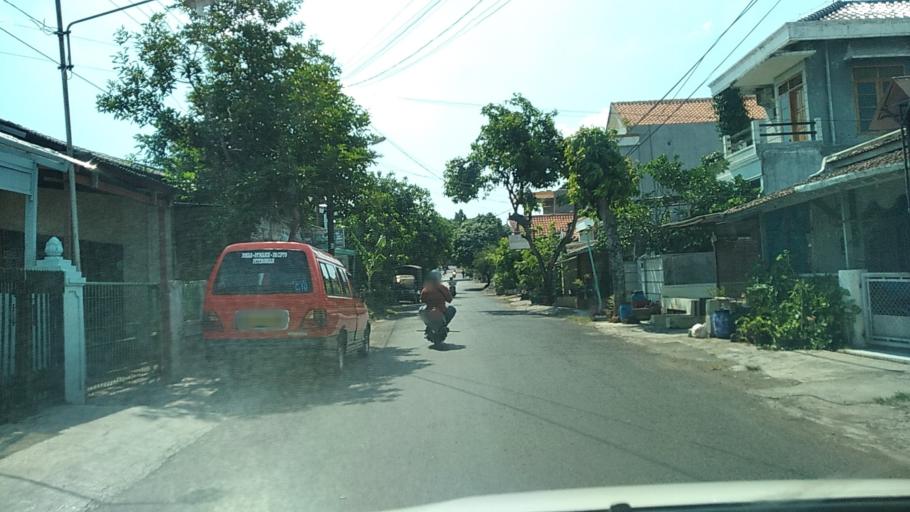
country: ID
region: Central Java
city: Ungaran
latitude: -7.0745
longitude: 110.4305
